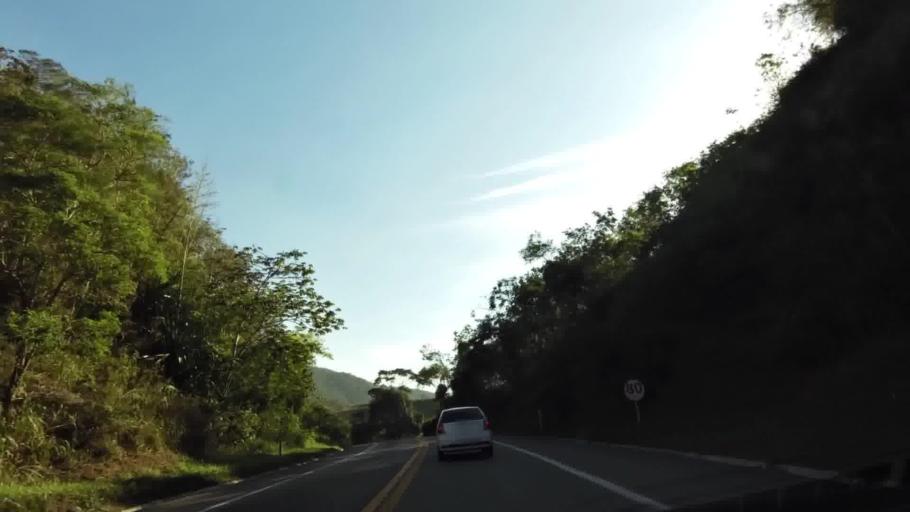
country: BR
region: Espirito Santo
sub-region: Viana
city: Viana
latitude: -20.4038
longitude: -40.4561
